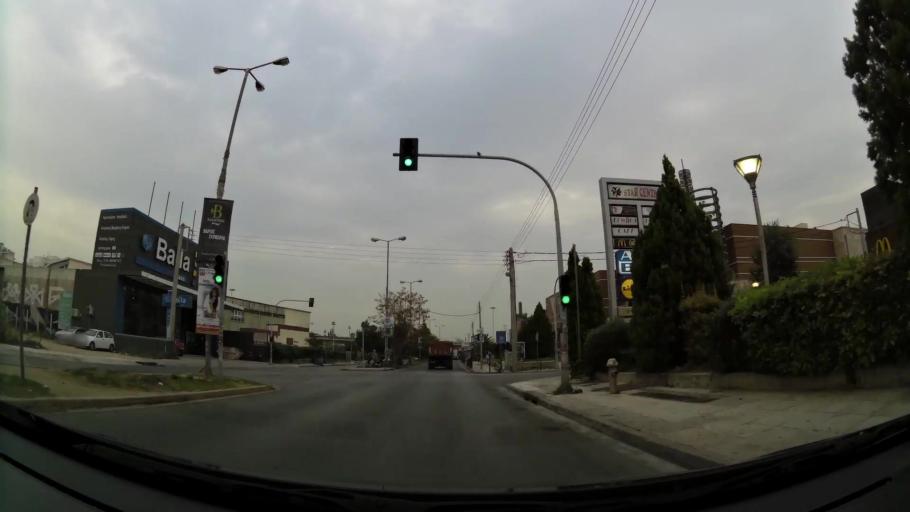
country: GR
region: Attica
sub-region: Nomos Piraios
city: Agios Ioannis Rentis
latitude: 37.9747
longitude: 23.6665
